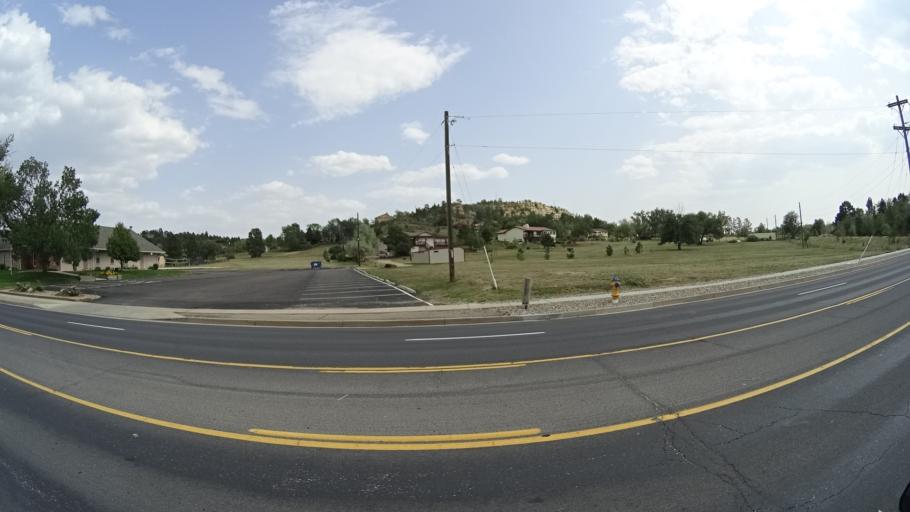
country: US
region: Colorado
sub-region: El Paso County
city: Cimarron Hills
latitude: 38.8604
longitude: -104.7480
